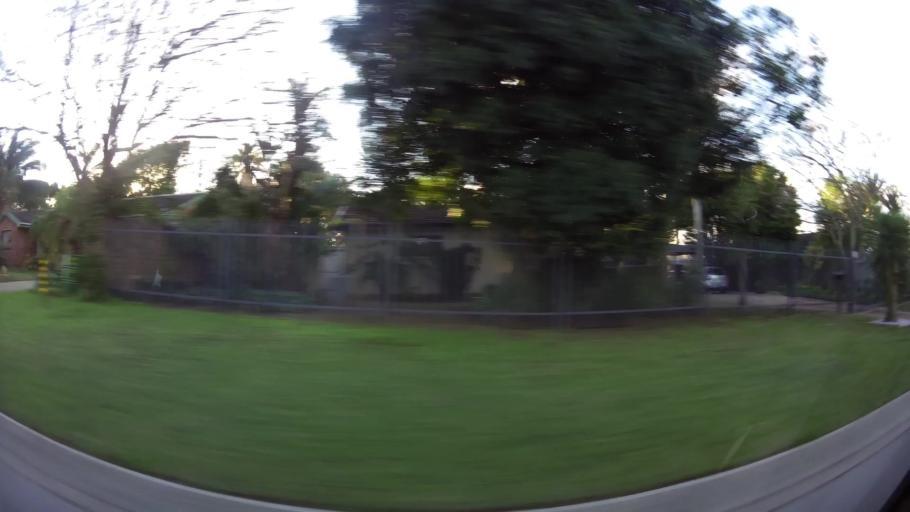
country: ZA
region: Eastern Cape
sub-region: Nelson Mandela Bay Metropolitan Municipality
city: Port Elizabeth
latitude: -33.9730
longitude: 25.4974
